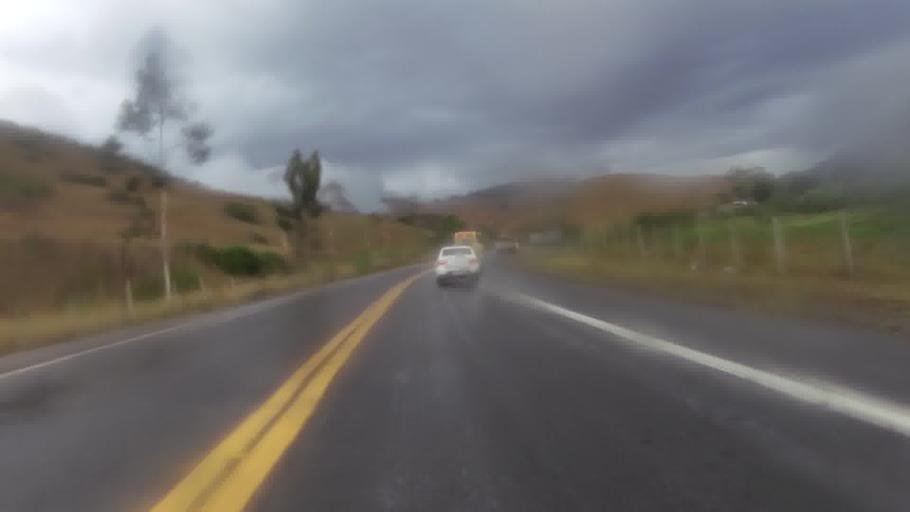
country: BR
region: Espirito Santo
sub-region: Cachoeiro De Itapemirim
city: Cachoeiro de Itapemirim
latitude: -20.9513
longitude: -41.0902
